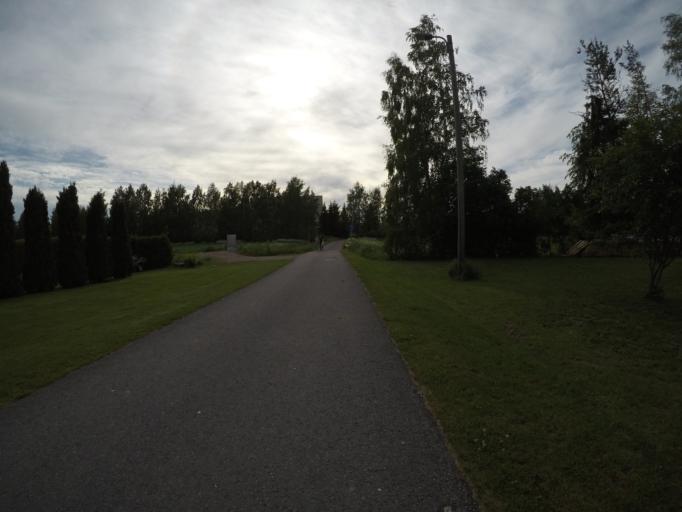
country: FI
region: Haeme
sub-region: Haemeenlinna
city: Haemeenlinna
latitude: 61.0089
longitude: 24.4233
